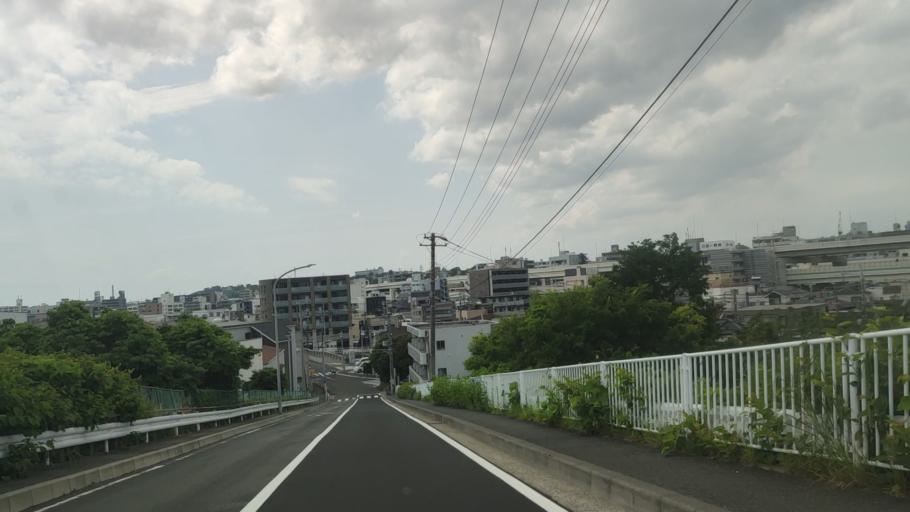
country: JP
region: Kanagawa
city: Yokohama
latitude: 35.4305
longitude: 139.6228
